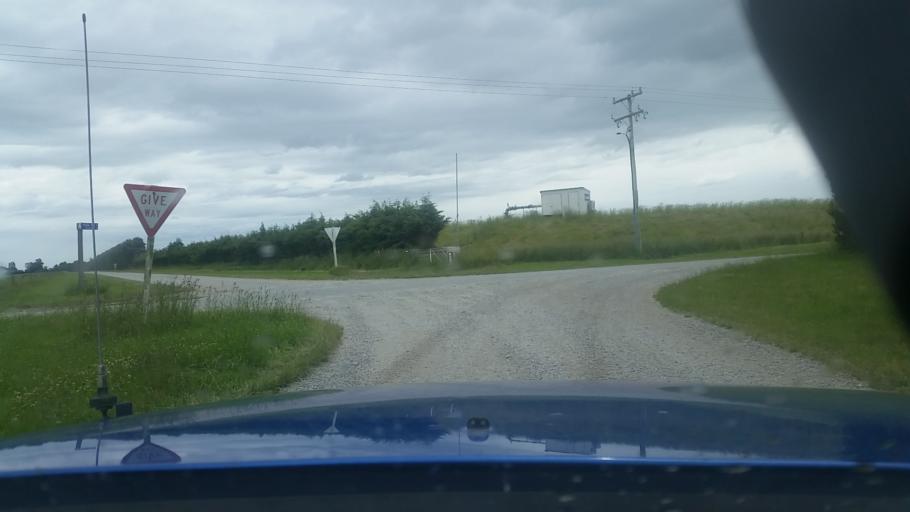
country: NZ
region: Canterbury
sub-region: Ashburton District
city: Rakaia
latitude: -43.9025
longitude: 172.0549
